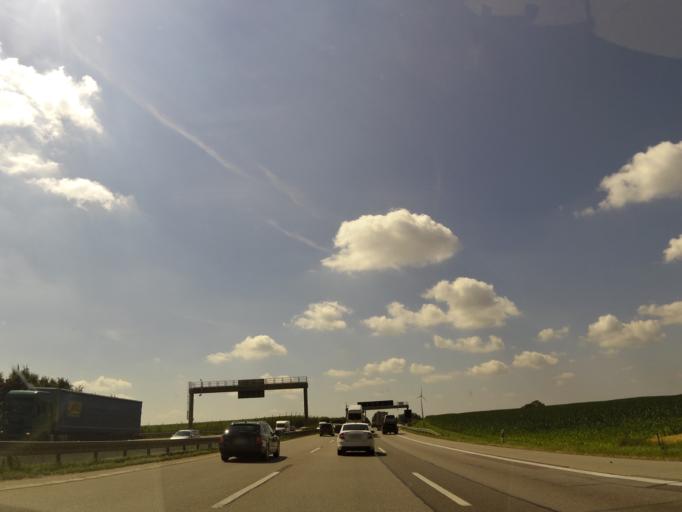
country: DE
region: Bavaria
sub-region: Upper Bavaria
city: Schweitenkirchen
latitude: 48.4964
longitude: 11.5947
